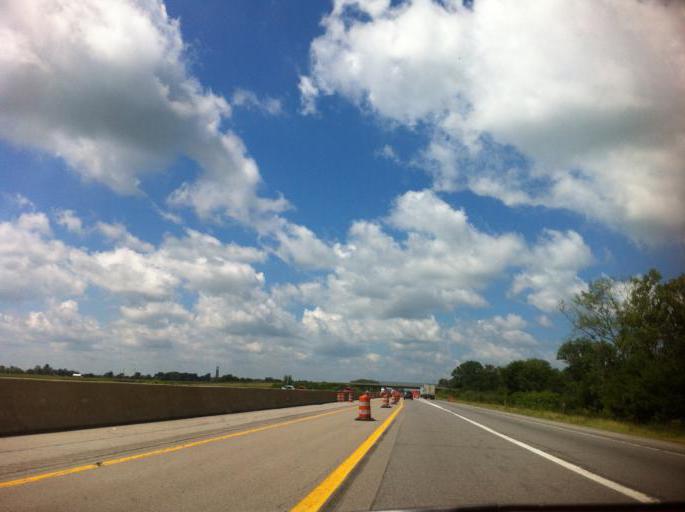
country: US
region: Ohio
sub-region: Huron County
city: Bellevue
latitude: 41.3477
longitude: -82.8113
